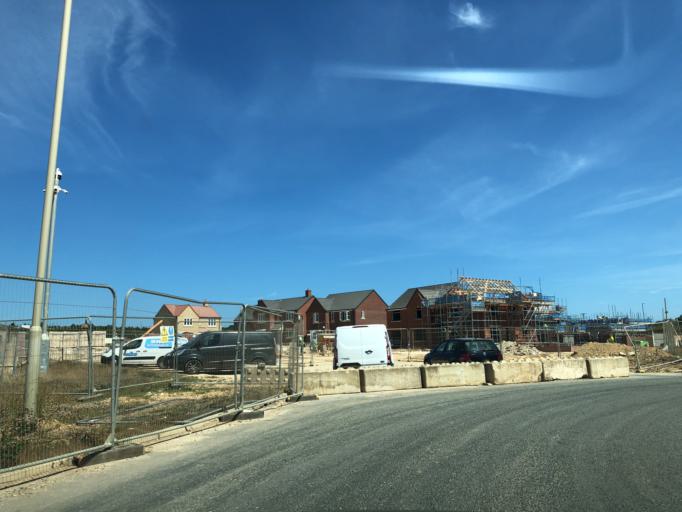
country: GB
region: England
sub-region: North Yorkshire
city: Scarborough
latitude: 54.2484
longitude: -0.3879
